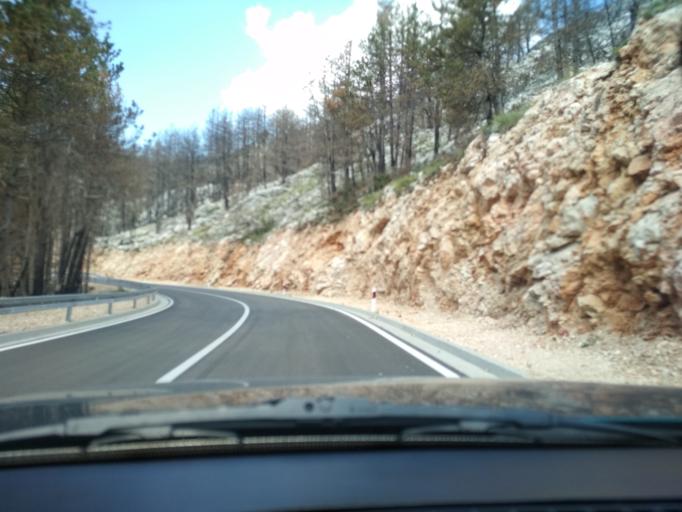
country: ME
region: Kotor
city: Kotor
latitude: 42.4368
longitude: 18.8415
